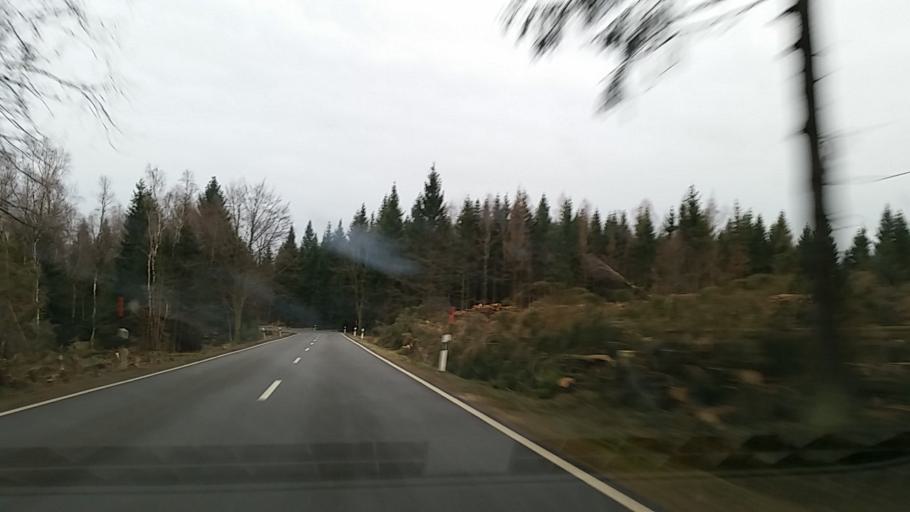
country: DE
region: Saxony-Anhalt
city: Benneckenstein
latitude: 51.6433
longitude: 10.6931
